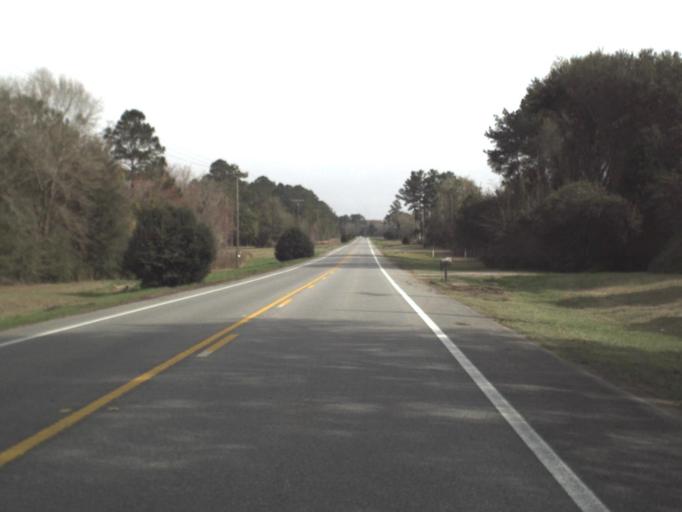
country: US
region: Florida
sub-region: Jefferson County
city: Monticello
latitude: 30.5146
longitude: -83.7794
